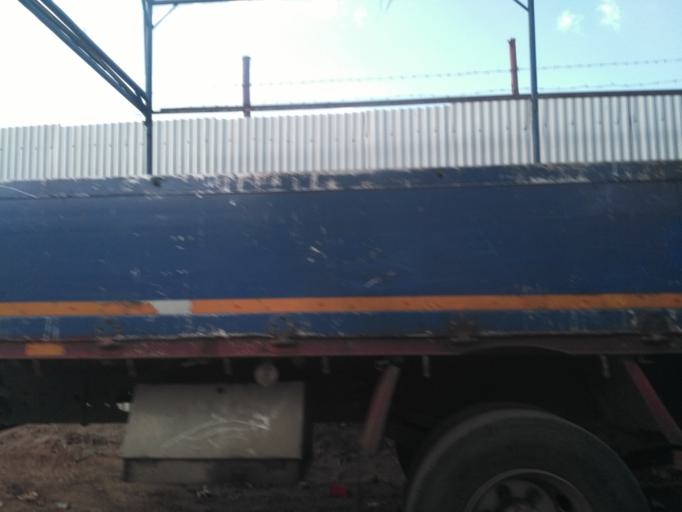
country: TZ
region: Dar es Salaam
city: Magomeni
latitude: -6.7832
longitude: 39.2649
